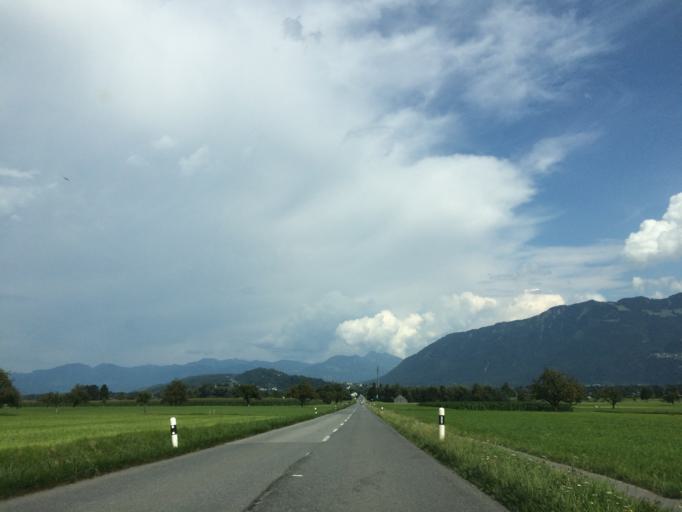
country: CH
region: Saint Gallen
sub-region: Wahlkreis Werdenberg
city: Gams
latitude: 47.2061
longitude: 9.4592
